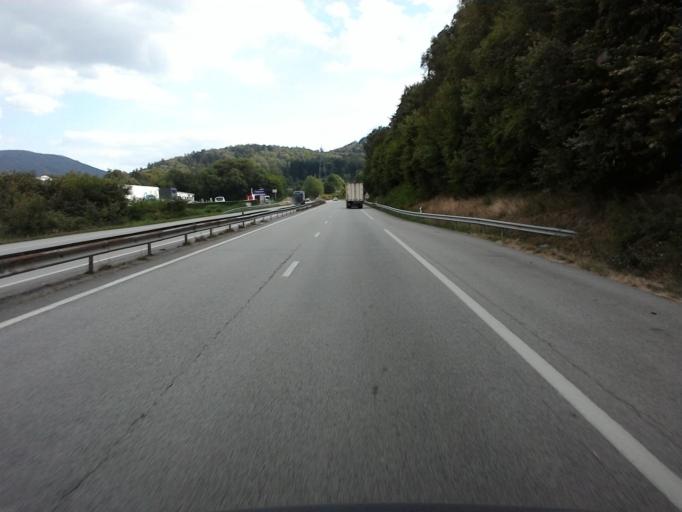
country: FR
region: Lorraine
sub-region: Departement des Vosges
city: Eloyes
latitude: 48.0777
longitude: 6.5939
